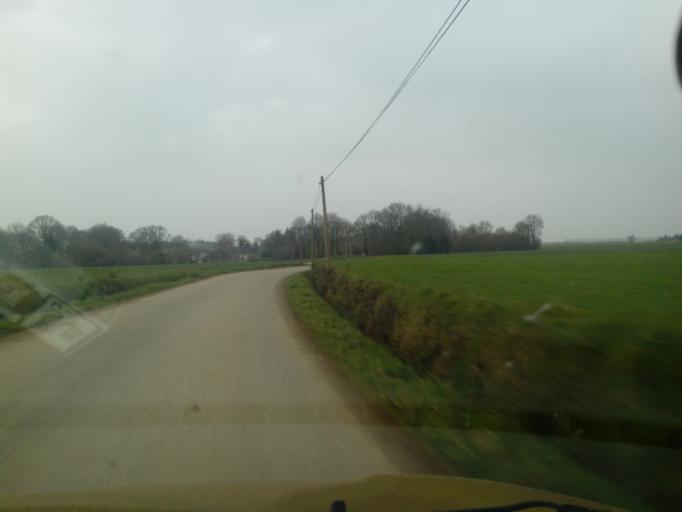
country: FR
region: Brittany
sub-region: Departement du Morbihan
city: Guilliers
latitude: 48.0607
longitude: -2.4007
